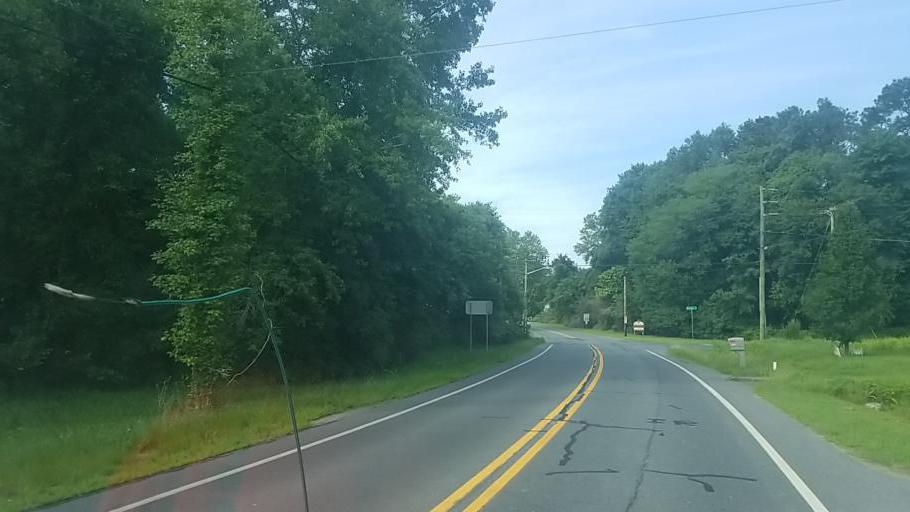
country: US
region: Delaware
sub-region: Sussex County
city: Selbyville
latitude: 38.5224
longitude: -75.2253
